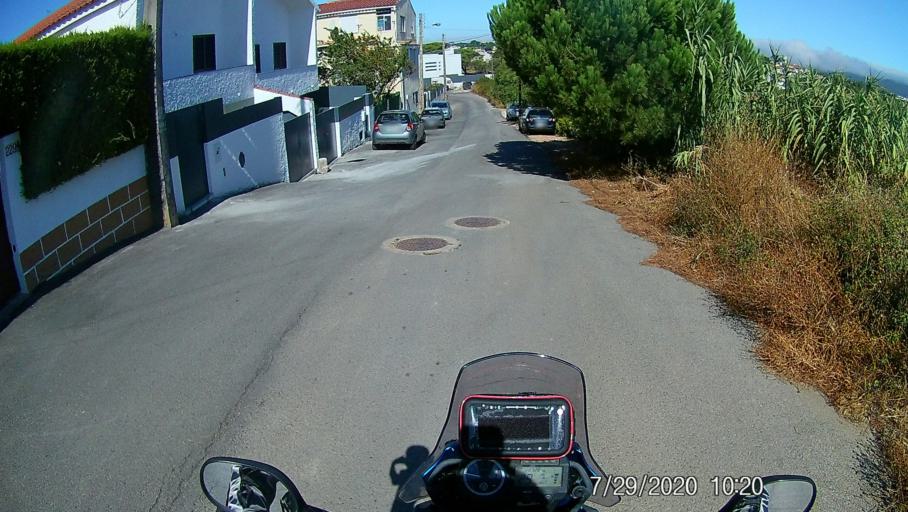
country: PT
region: Lisbon
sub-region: Cascais
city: Estoril
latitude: 38.7260
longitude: -9.3774
